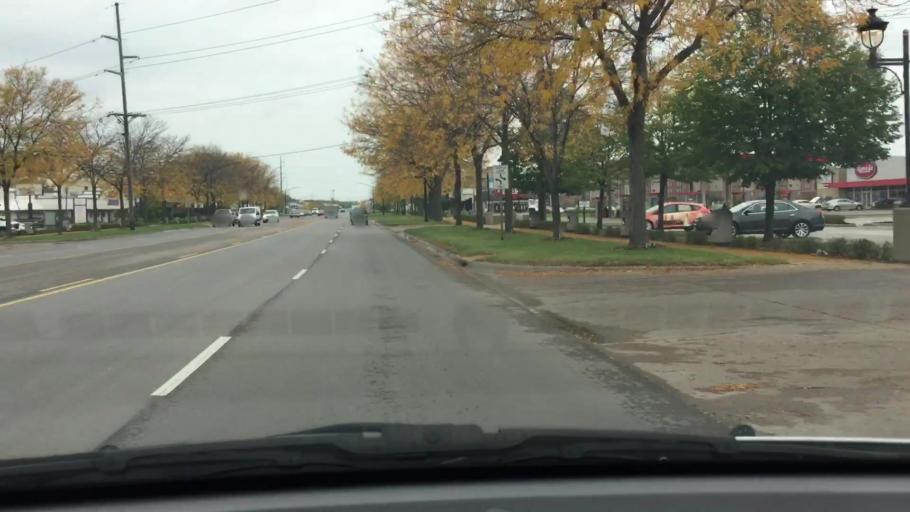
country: US
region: Iowa
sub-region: Johnson County
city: Coralville
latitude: 41.6696
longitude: -91.5670
